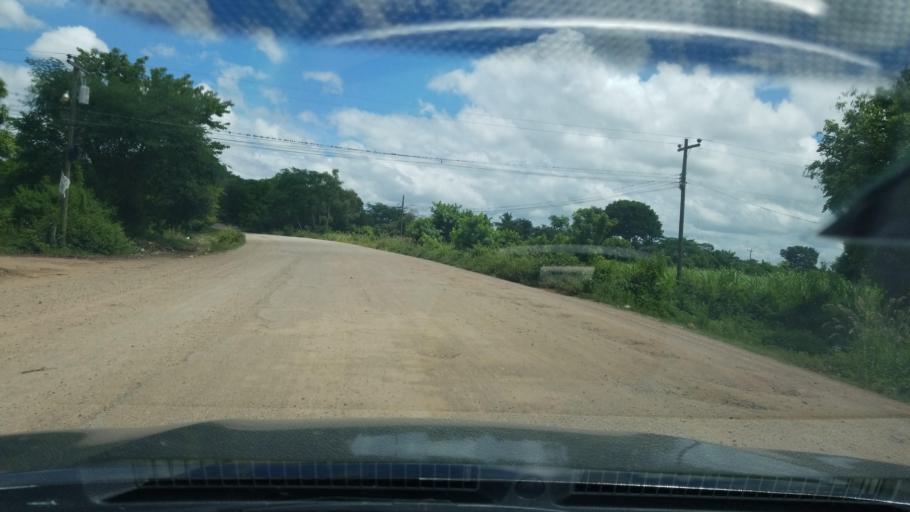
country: HN
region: Francisco Morazan
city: Talanga
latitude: 14.3701
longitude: -87.0558
